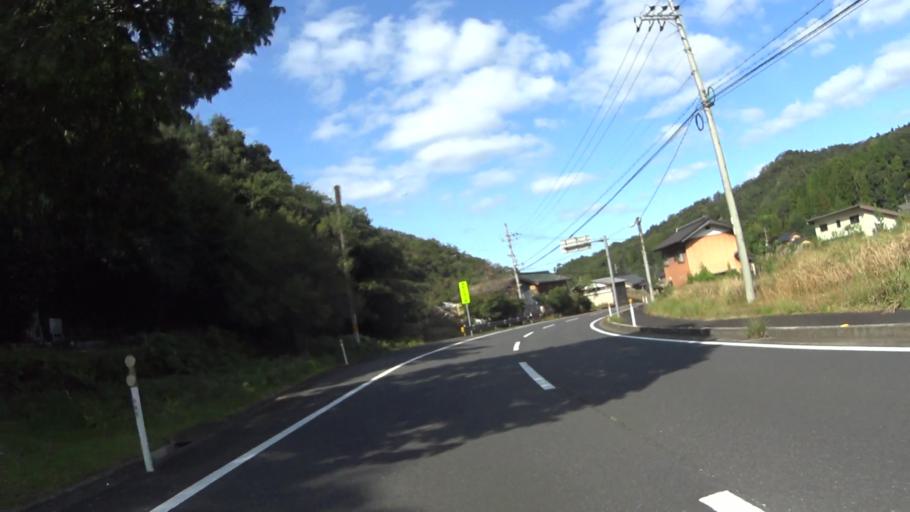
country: JP
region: Hyogo
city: Toyooka
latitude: 35.5607
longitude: 134.9789
